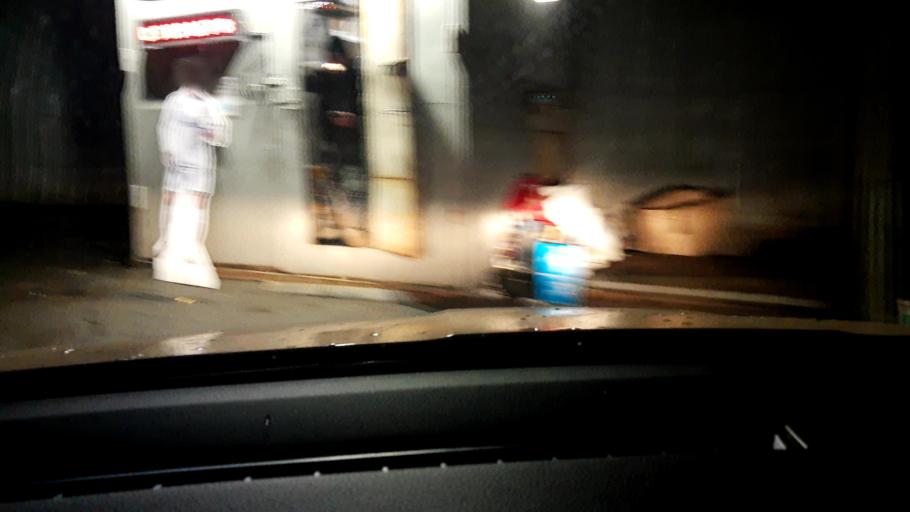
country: RU
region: Moscow
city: Mar'ina Roshcha
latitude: 55.8081
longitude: 37.6037
